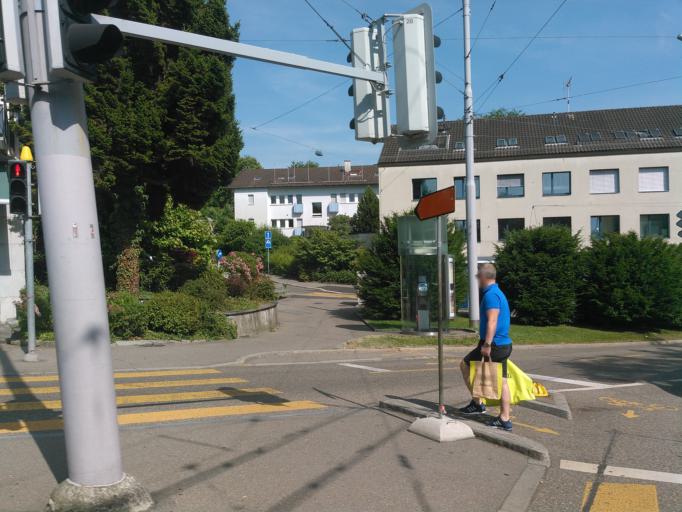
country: CH
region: Zurich
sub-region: Bezirk Zuerich
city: Zuerich (Kreis 7) / Fluntern
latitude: 47.3769
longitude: 8.5598
